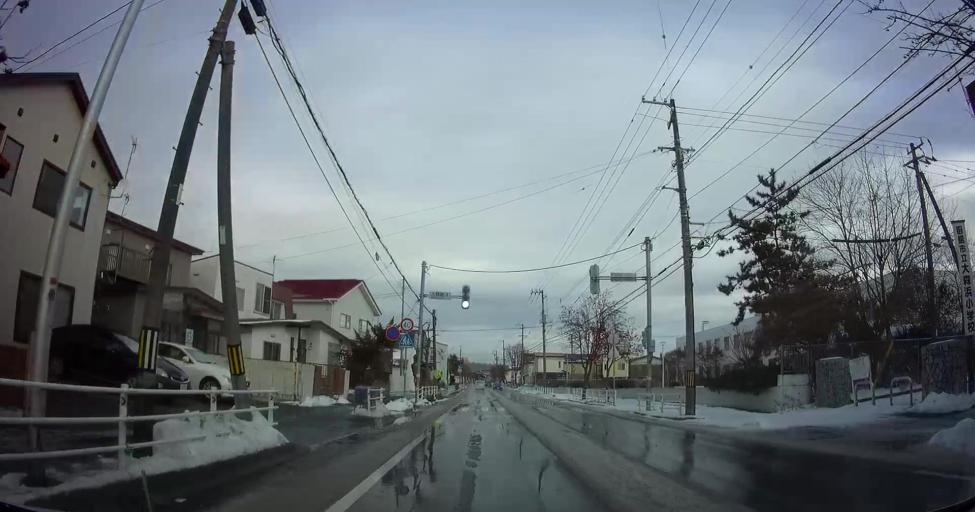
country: JP
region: Hokkaido
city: Hakodate
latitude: 41.7786
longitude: 140.7563
